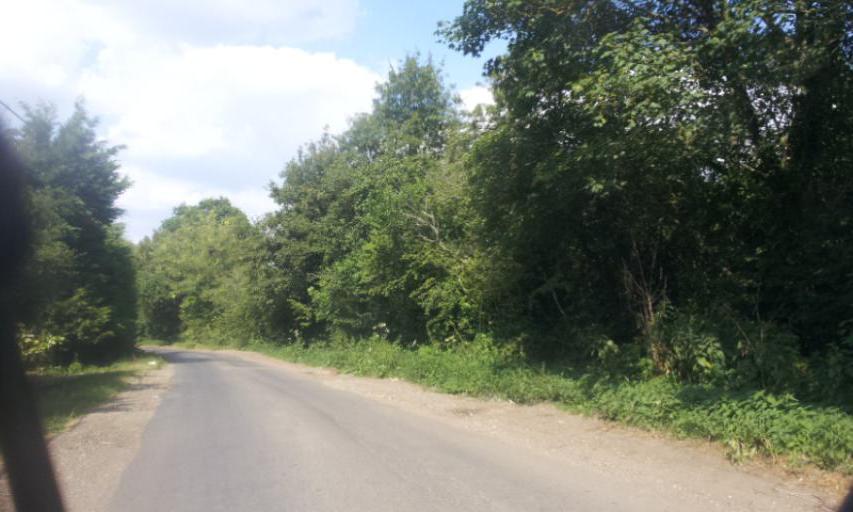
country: GB
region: England
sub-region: Kent
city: Yalding
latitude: 51.1924
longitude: 0.4199
